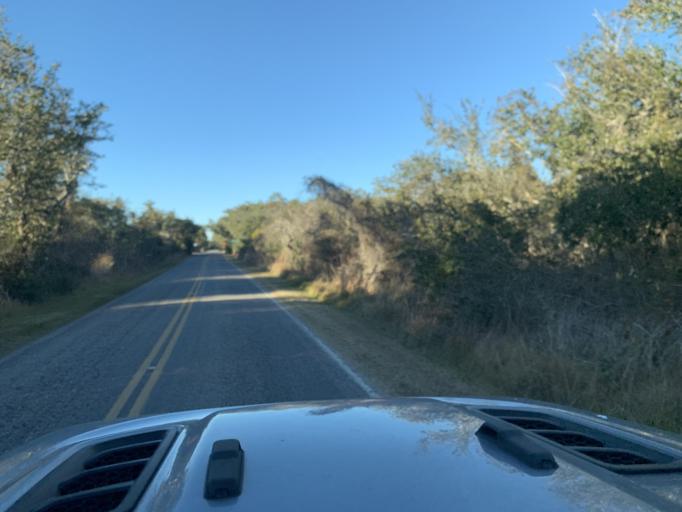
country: US
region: Texas
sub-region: Aransas County
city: Fulton
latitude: 28.1502
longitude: -96.9843
